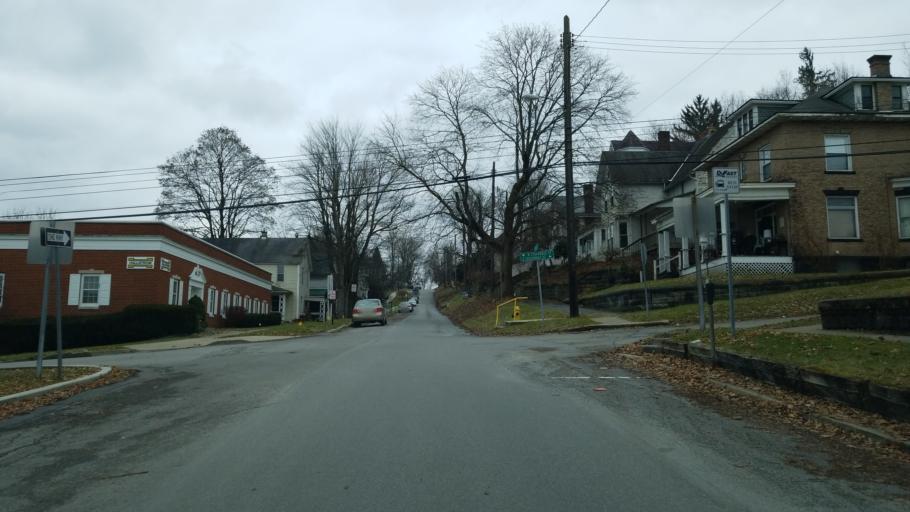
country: US
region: Pennsylvania
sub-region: Clearfield County
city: DuBois
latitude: 41.1176
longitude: -78.7612
